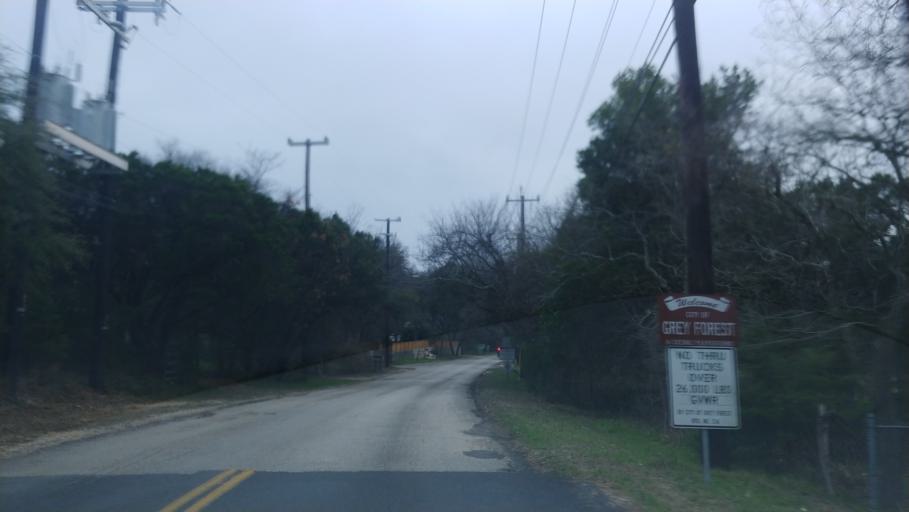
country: US
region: Texas
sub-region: Bexar County
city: Cross Mountain
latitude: 29.6273
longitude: -98.6829
